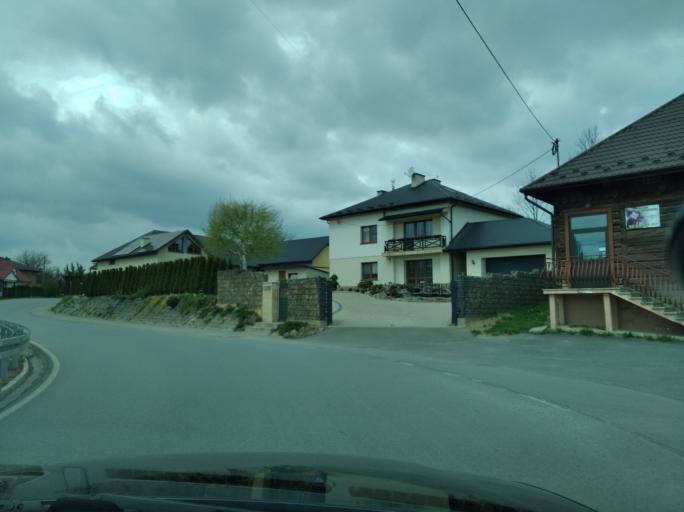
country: PL
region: Subcarpathian Voivodeship
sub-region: Powiat brzozowski
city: Jablonica Polska
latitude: 49.6979
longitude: 21.9008
